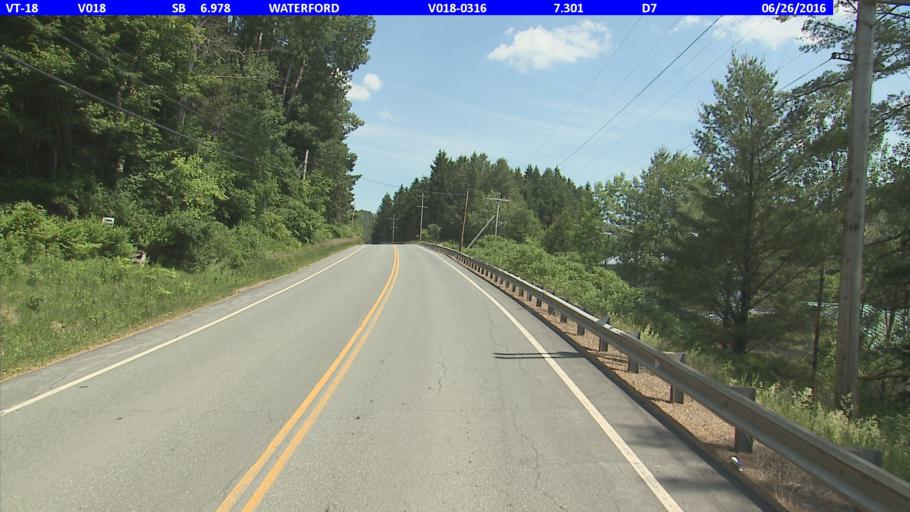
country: US
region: Vermont
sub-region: Caledonia County
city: St Johnsbury
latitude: 44.4231
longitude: -71.9481
